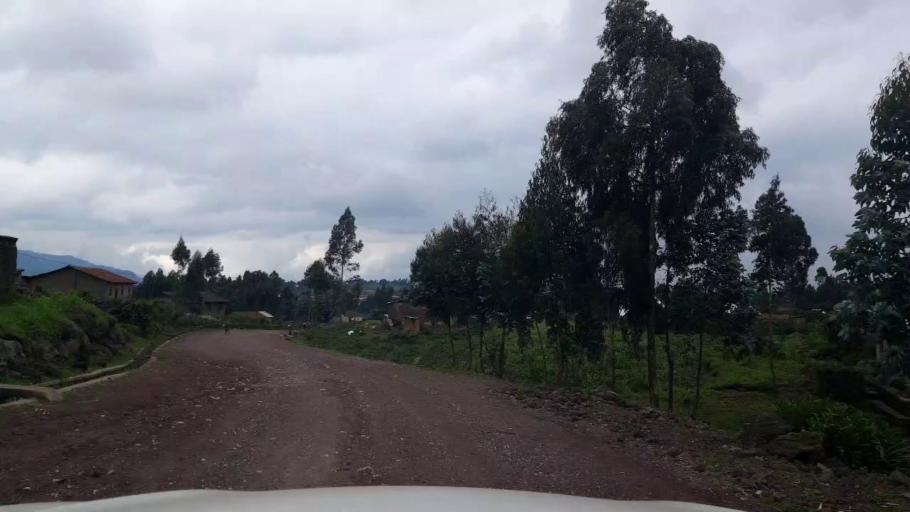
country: RW
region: Northern Province
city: Musanze
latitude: -1.5913
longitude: 29.4612
